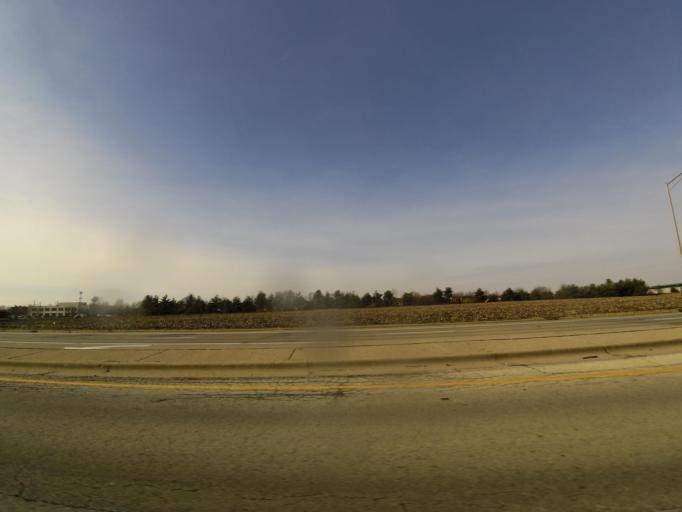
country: US
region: Illinois
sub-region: Macon County
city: Forsyth
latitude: 39.9257
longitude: -88.9555
